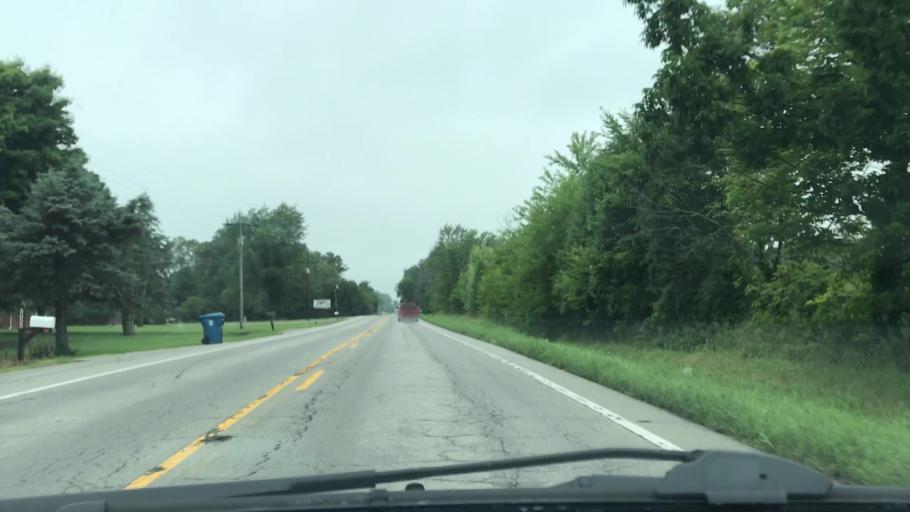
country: US
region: Indiana
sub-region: Hamilton County
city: Westfield
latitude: 40.0835
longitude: -86.1025
